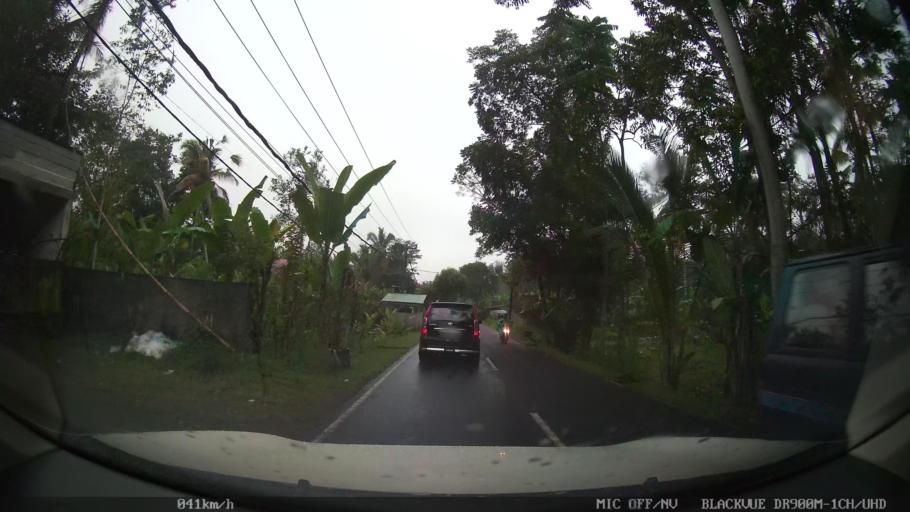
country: ID
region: Bali
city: Banjar Taro Kelod
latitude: -8.3702
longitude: 115.2694
